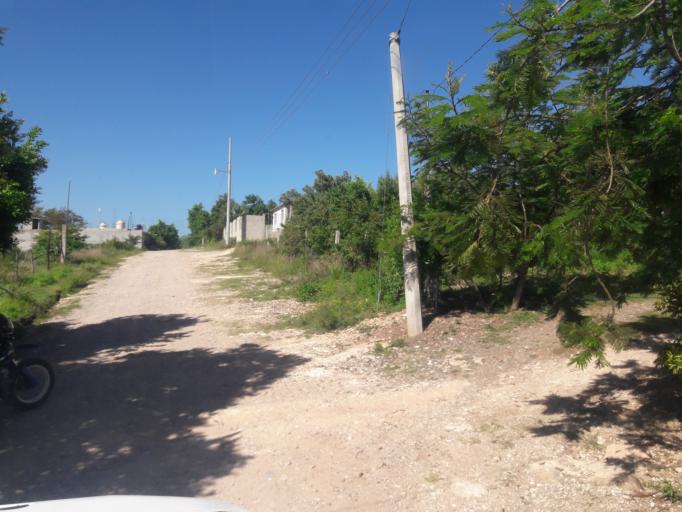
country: MX
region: Oaxaca
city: Ciudad de Huajuapam de Leon
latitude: 17.8048
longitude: -97.8056
